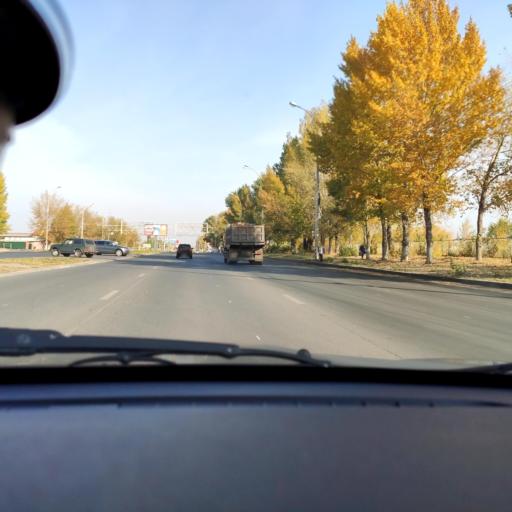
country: RU
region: Samara
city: Tol'yatti
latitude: 53.5392
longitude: 49.2843
